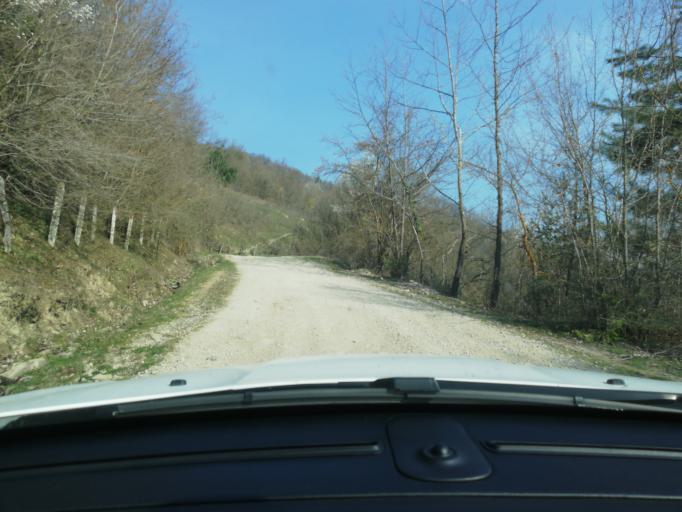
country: TR
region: Karabuk
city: Yenice
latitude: 41.2639
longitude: 32.3603
